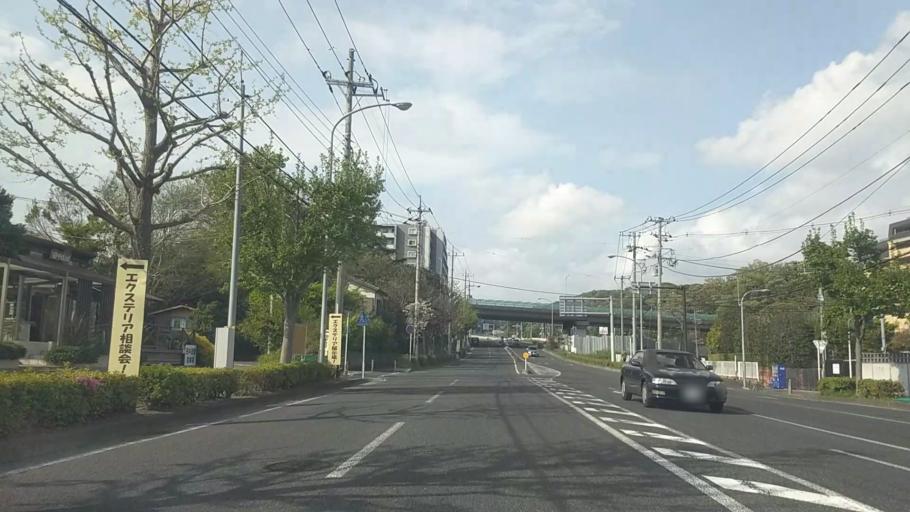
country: JP
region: Kanagawa
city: Kamakura
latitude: 35.3767
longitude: 139.5522
